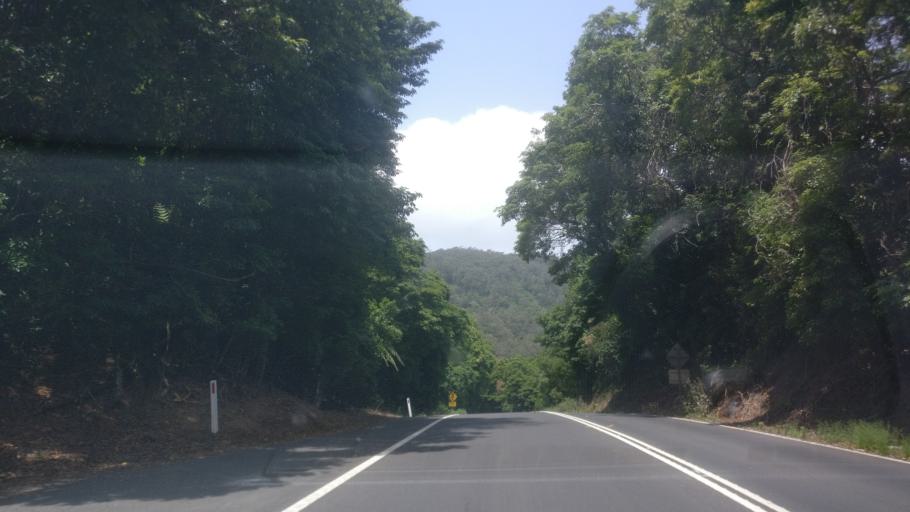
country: AU
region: New South Wales
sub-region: Shoalhaven Shire
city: Kangaroo Valley
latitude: -34.7913
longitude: 150.5618
